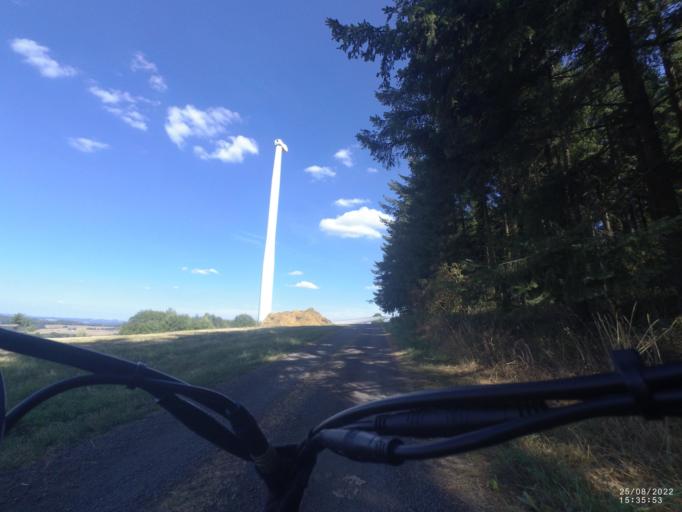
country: DE
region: Rheinland-Pfalz
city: Hohenfels-Essingen
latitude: 50.2674
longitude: 6.7308
